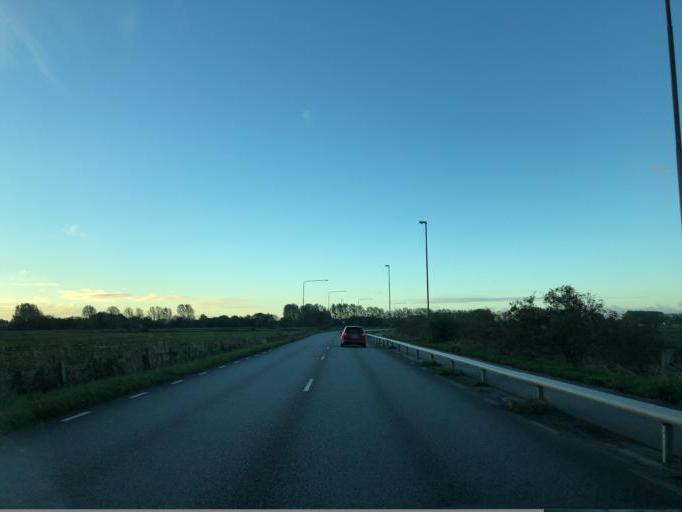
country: SE
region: Skane
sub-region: Burlovs Kommun
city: Arloev
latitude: 55.6468
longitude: 13.0587
